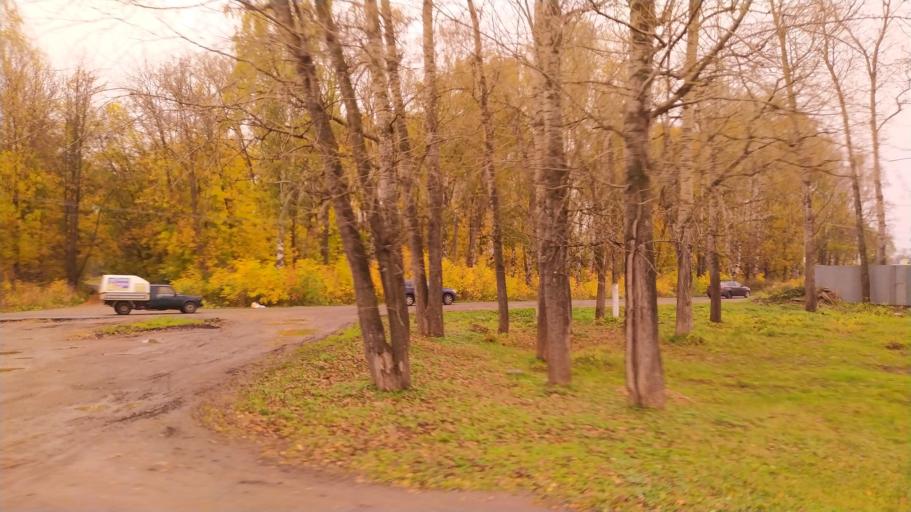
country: RU
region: Tverskaya
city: Tver
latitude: 56.8294
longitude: 35.8926
